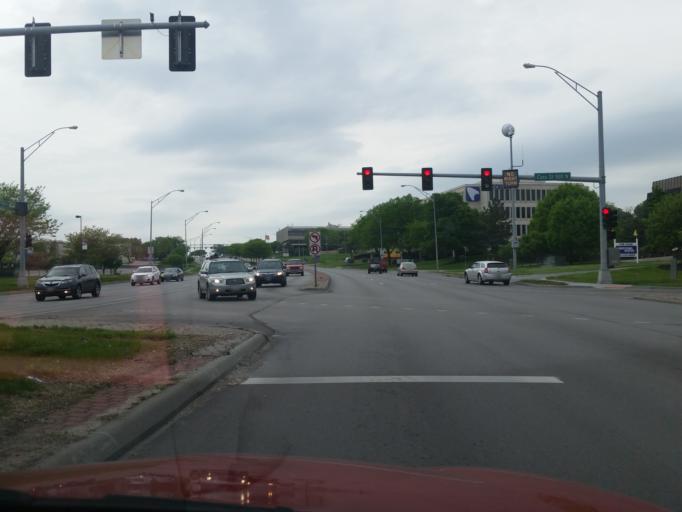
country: US
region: Nebraska
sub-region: Douglas County
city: Ralston
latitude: 41.2630
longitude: -96.0465
